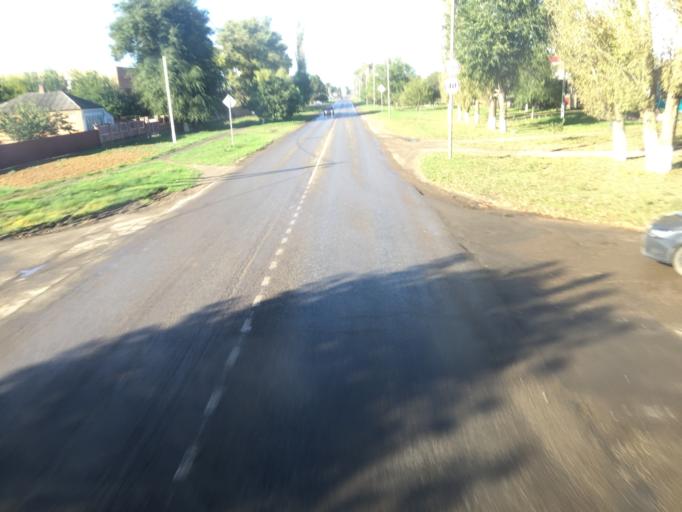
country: RU
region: Rostov
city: Peschanokopskoye
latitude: 46.1925
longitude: 41.0961
